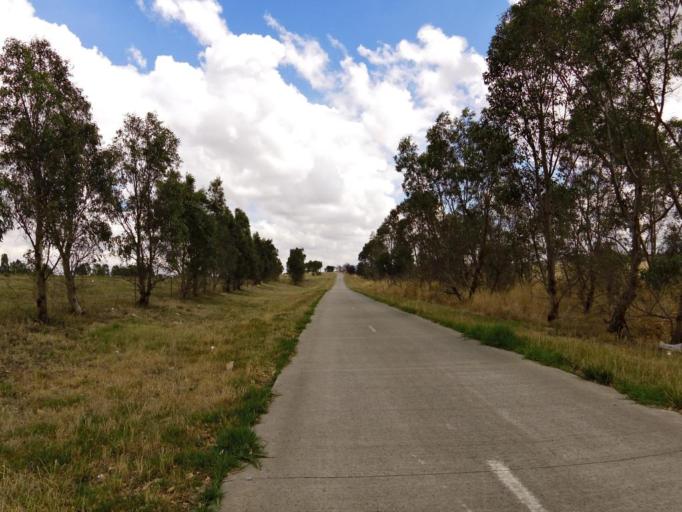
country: AU
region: Victoria
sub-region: Hume
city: Craigieburn
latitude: -37.6116
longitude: 144.9856
